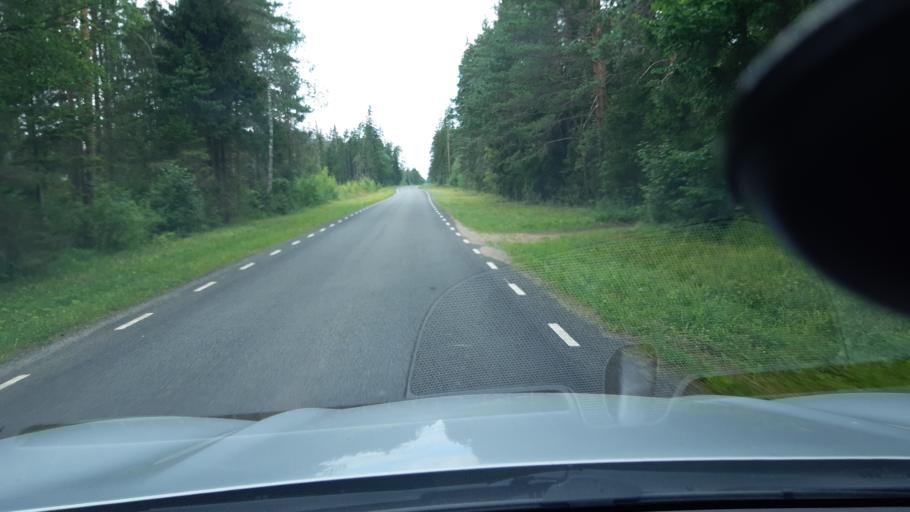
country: EE
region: Raplamaa
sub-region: Rapla vald
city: Rapla
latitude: 58.8910
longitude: 24.7144
